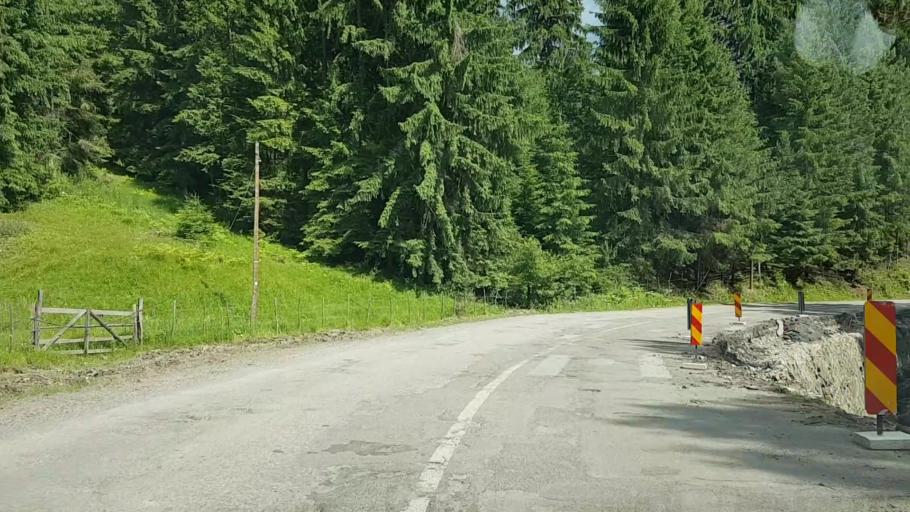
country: RO
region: Neamt
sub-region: Comuna Hangu
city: Hangu
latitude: 47.0507
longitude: 26.0079
